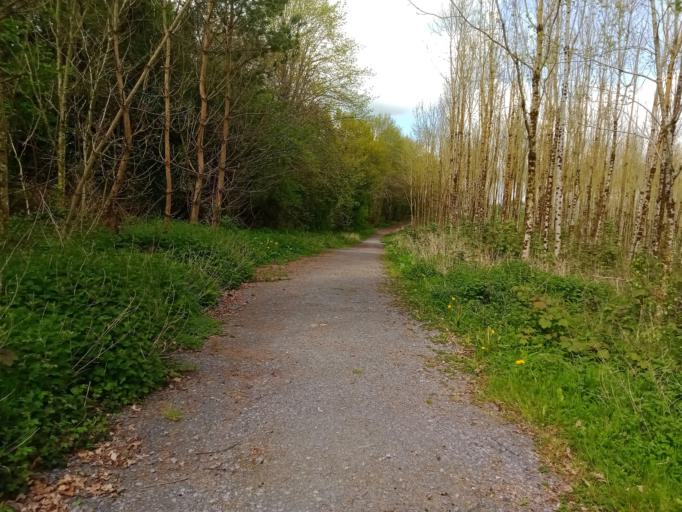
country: IE
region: Leinster
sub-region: Kilkenny
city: Ballyragget
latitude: 52.7271
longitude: -7.4147
